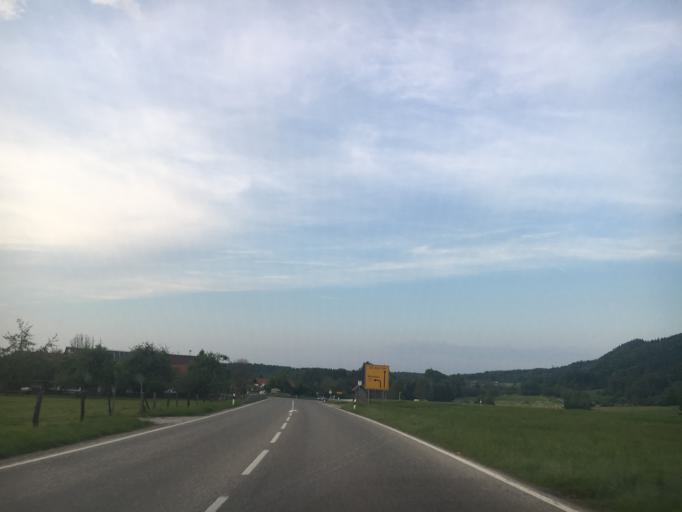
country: DE
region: Bavaria
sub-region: Upper Bavaria
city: Bichl
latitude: 47.7284
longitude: 11.4285
